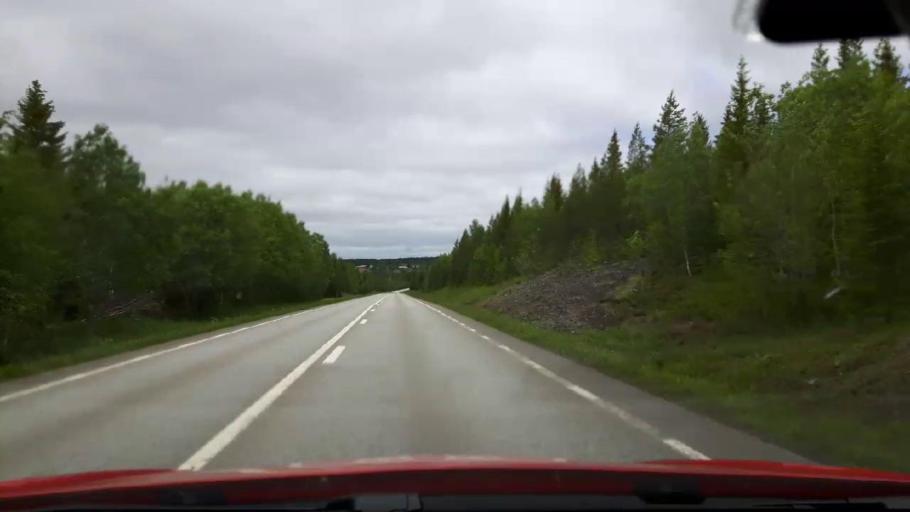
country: SE
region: Jaemtland
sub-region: Krokoms Kommun
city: Krokom
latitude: 63.5030
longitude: 14.5146
